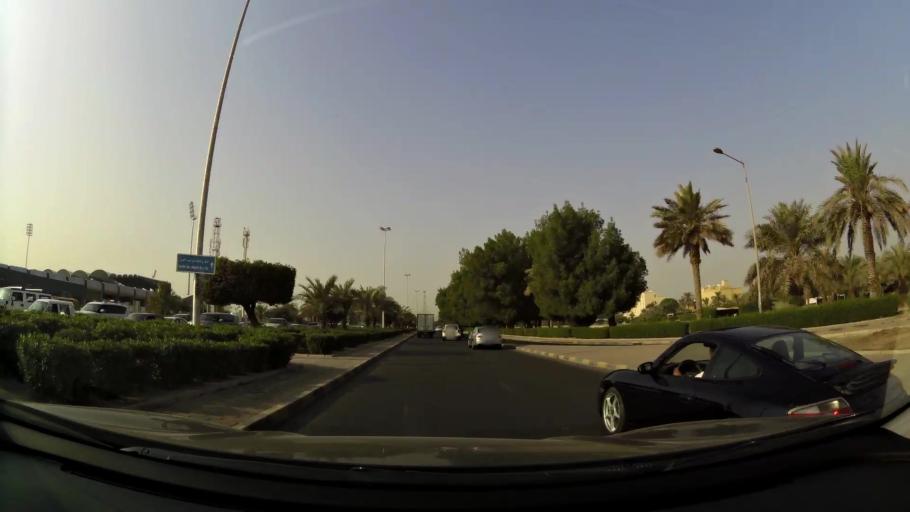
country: KW
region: Muhafazat Hawalli
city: Salwa
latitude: 29.2931
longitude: 48.0688
